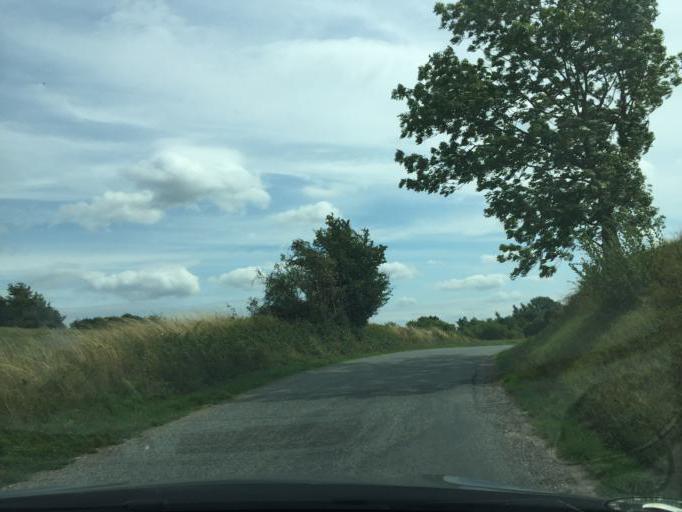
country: DK
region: South Denmark
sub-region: Assens Kommune
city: Tommerup Stationsby
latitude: 55.3962
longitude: 10.2436
